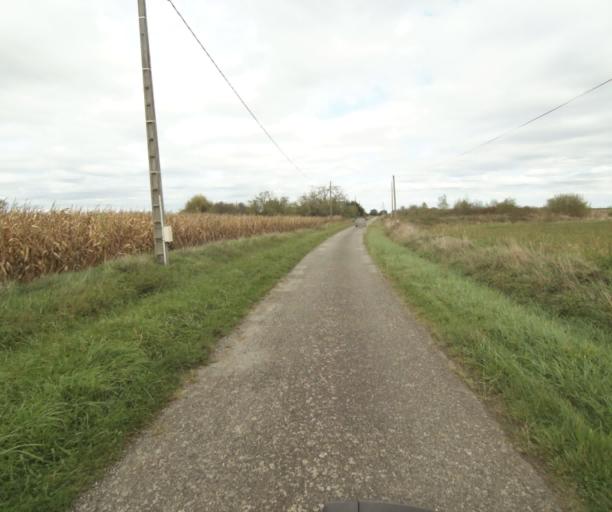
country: FR
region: Midi-Pyrenees
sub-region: Departement du Tarn-et-Garonne
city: Verdun-sur-Garonne
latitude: 43.8641
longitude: 1.1503
